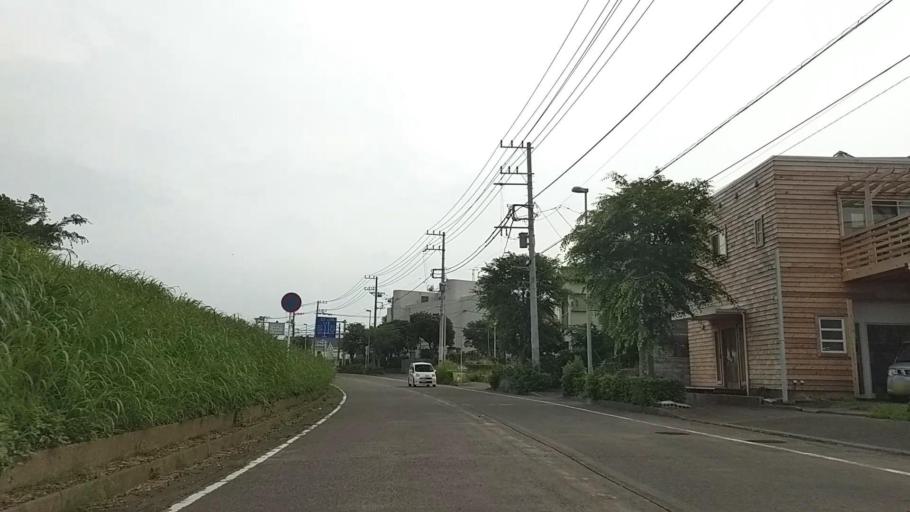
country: JP
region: Kanagawa
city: Hiratsuka
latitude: 35.3199
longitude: 139.3308
